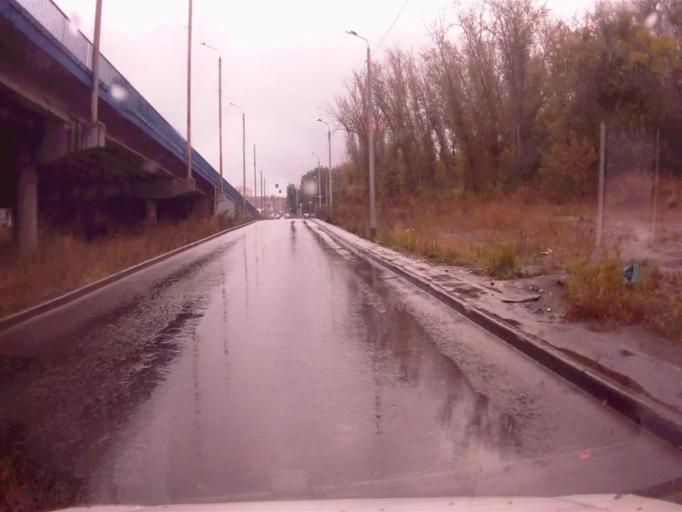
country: RU
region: Chelyabinsk
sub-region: Gorod Chelyabinsk
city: Chelyabinsk
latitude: 55.1958
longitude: 61.3876
